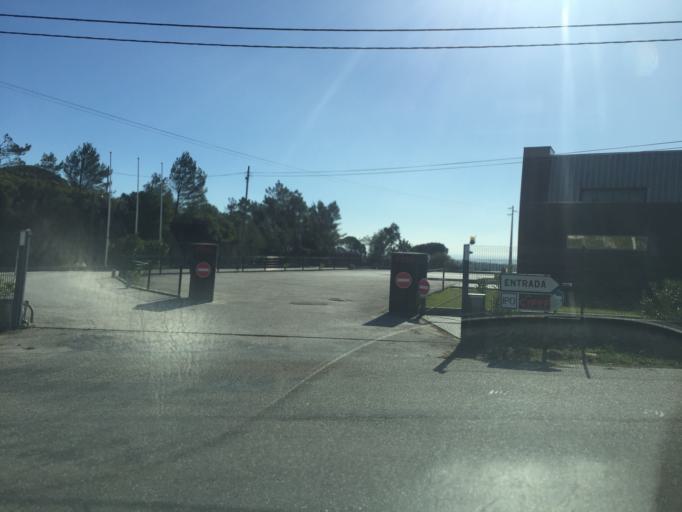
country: PT
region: Coimbra
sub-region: Figueira da Foz
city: Tavarede
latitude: 40.1896
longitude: -8.8308
